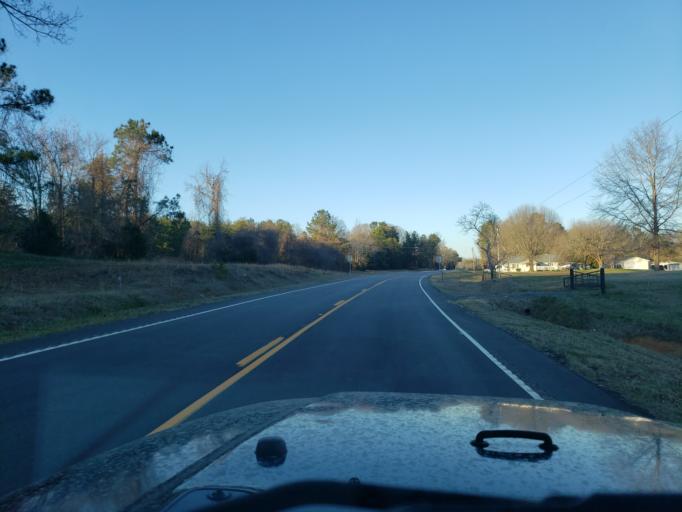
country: US
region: South Carolina
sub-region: Cherokee County
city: Blacksburg
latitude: 35.0194
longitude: -81.4057
